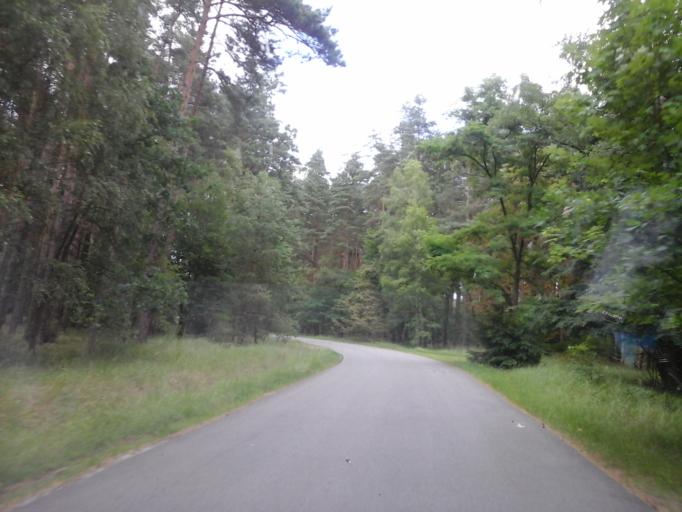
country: PL
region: West Pomeranian Voivodeship
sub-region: Powiat goleniowski
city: Goleniow
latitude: 53.4574
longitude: 14.7919
